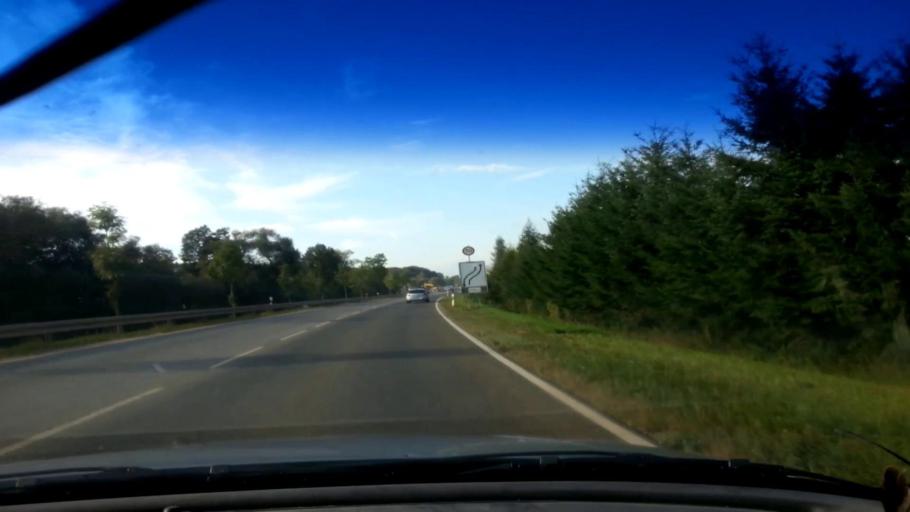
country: DE
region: Bavaria
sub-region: Upper Franconia
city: Baunach
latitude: 49.9742
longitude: 10.8629
